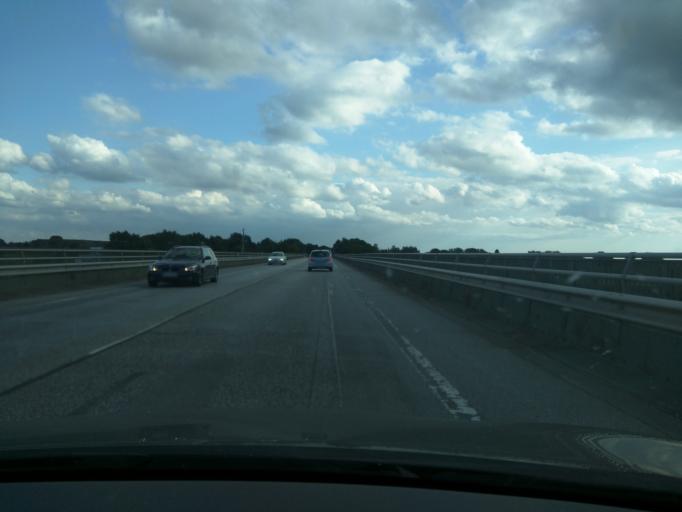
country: DE
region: Lower Saxony
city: Marschacht
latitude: 53.4252
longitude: 10.3362
